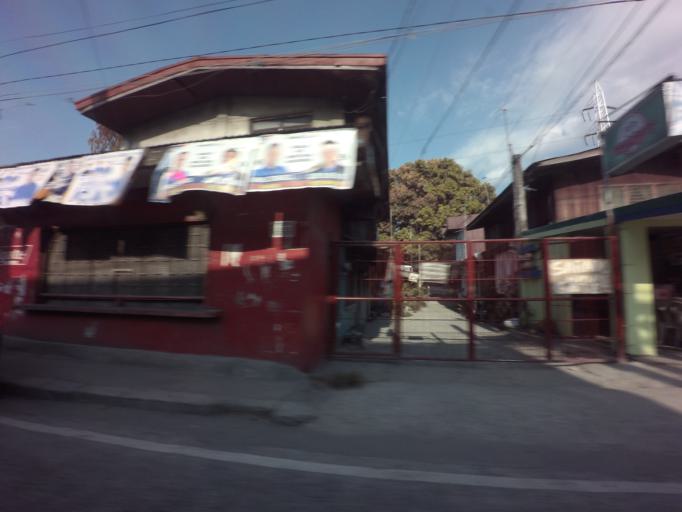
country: PH
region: Calabarzon
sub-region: Province of Rizal
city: Taguig
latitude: 14.4785
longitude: 121.0609
